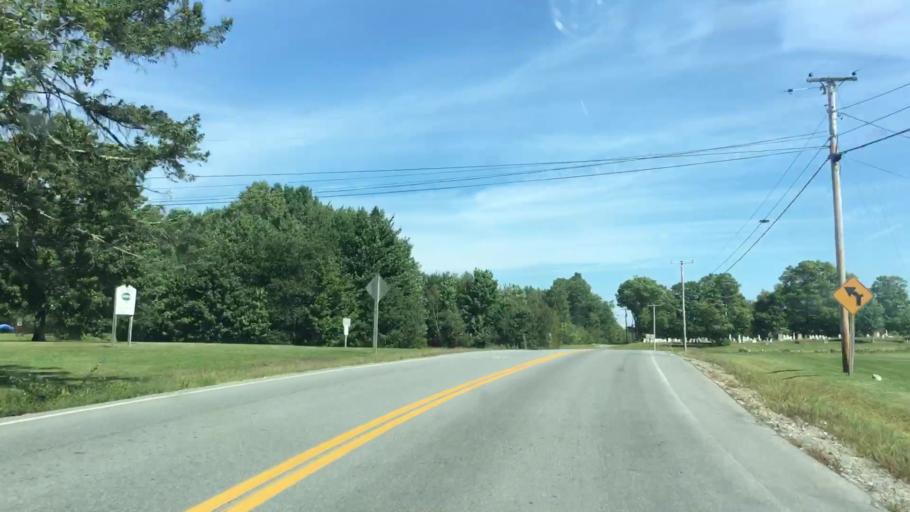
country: US
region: Maine
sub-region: Penobscot County
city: Bradford
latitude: 45.1661
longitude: -68.8435
